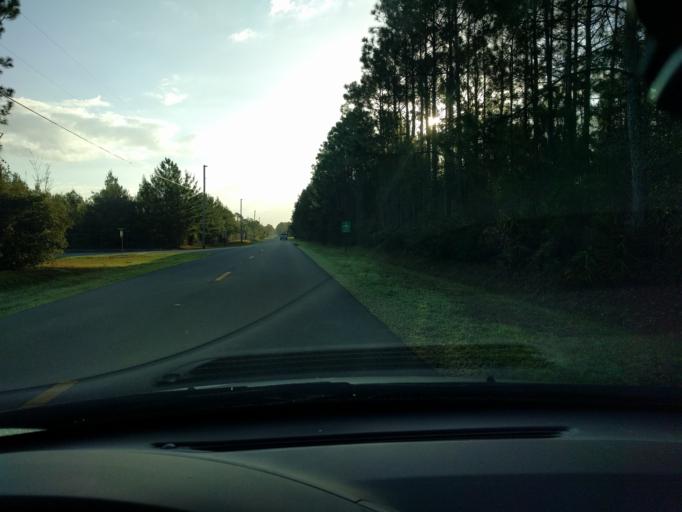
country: US
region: Florida
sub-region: Franklin County
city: Apalachicola
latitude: 29.7176
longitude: -85.0252
